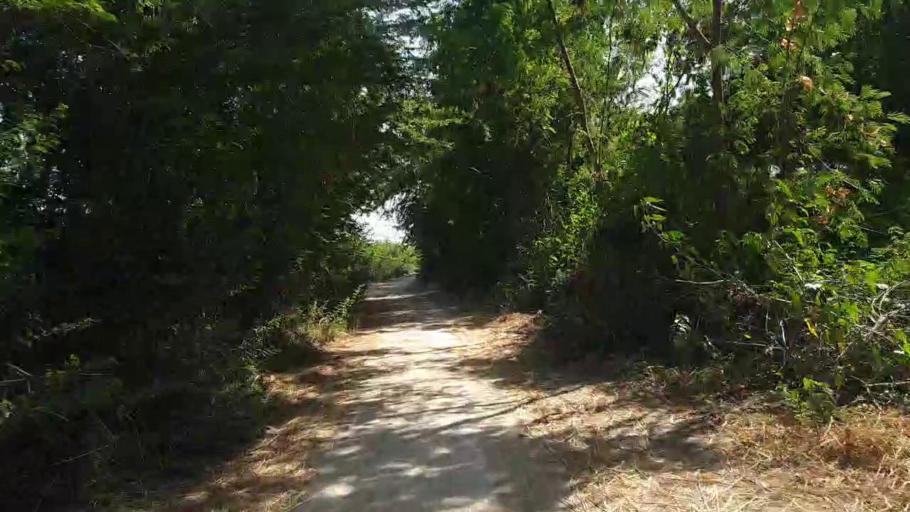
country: PK
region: Sindh
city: Tando Bago
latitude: 24.6485
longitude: 68.9848
